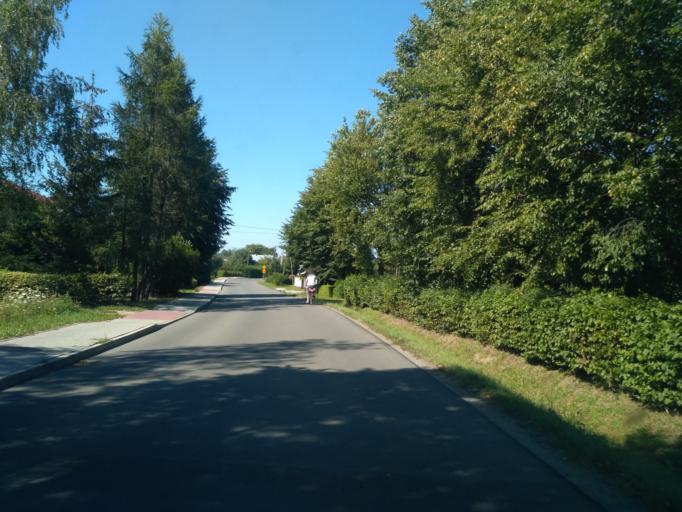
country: PL
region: Subcarpathian Voivodeship
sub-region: Powiat krosnienski
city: Miejsce Piastowe
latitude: 49.6367
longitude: 21.7459
